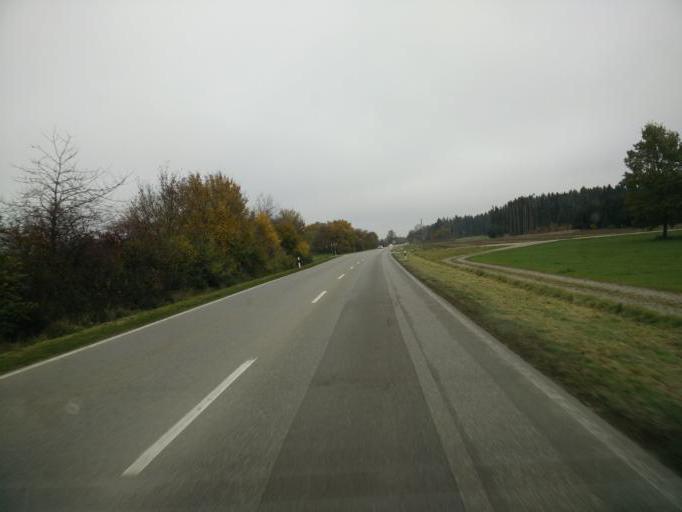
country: DE
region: Bavaria
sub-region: Swabia
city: Bad Worishofen
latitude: 48.0226
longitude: 10.6102
